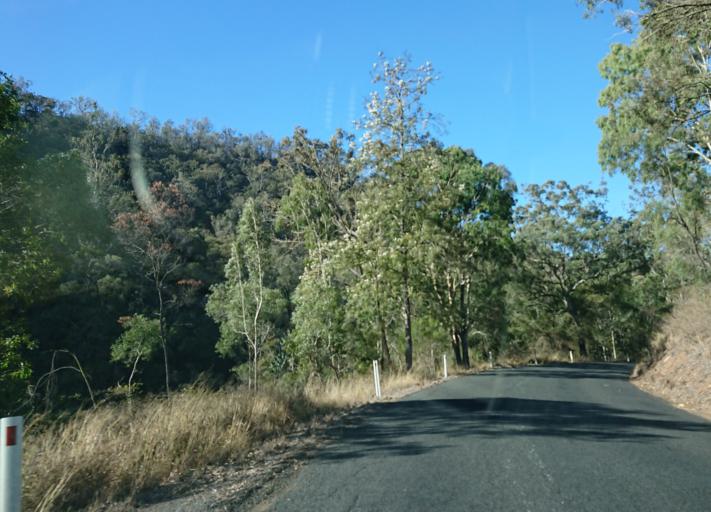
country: AU
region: Queensland
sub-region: Toowoomba
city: Top Camp
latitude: -27.7483
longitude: 152.0855
